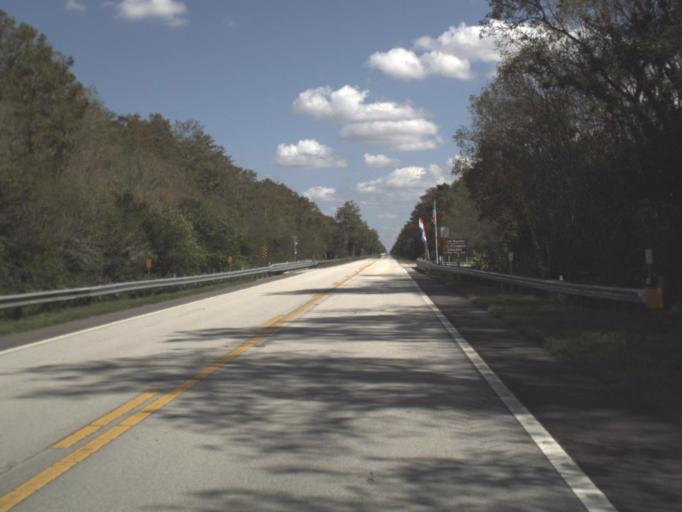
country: US
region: Florida
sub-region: Miami-Dade County
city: Kendall West
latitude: 25.8556
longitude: -81.0211
